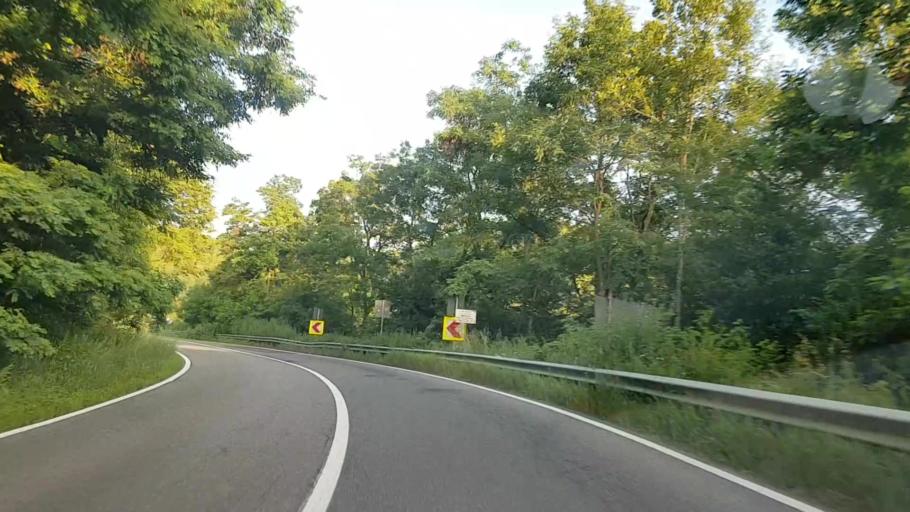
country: RO
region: Harghita
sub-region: Comuna Corund
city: Corund
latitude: 46.4514
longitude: 25.2133
